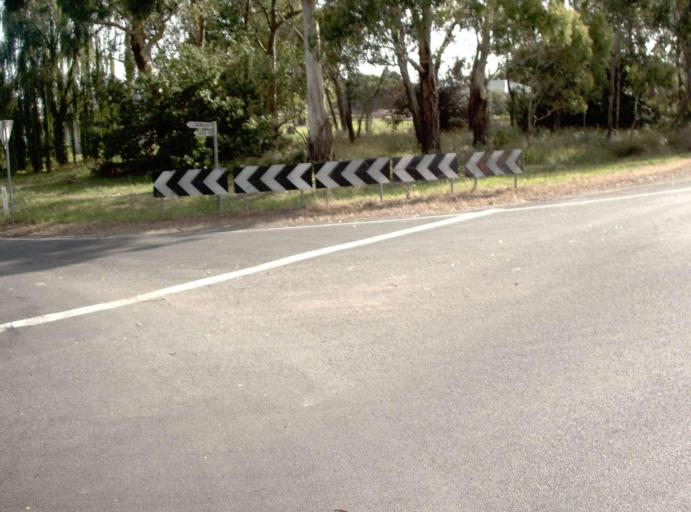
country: AU
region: Victoria
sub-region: Cardinia
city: Bunyip
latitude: -38.0817
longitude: 145.7784
